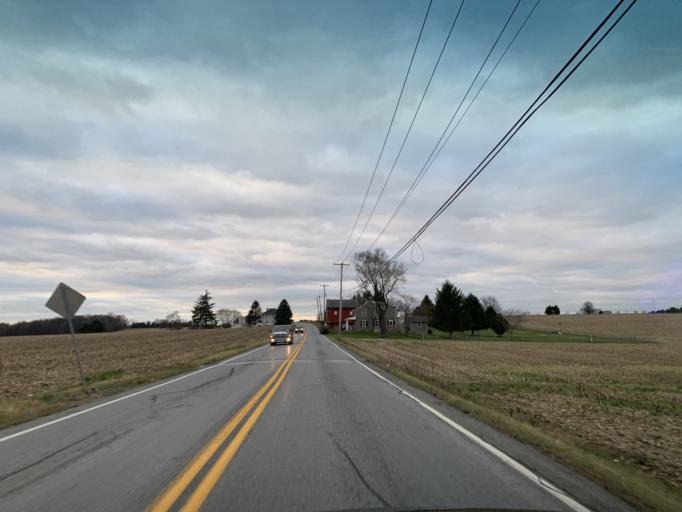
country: US
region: Pennsylvania
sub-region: York County
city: Shrewsbury
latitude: 39.7845
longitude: -76.6458
